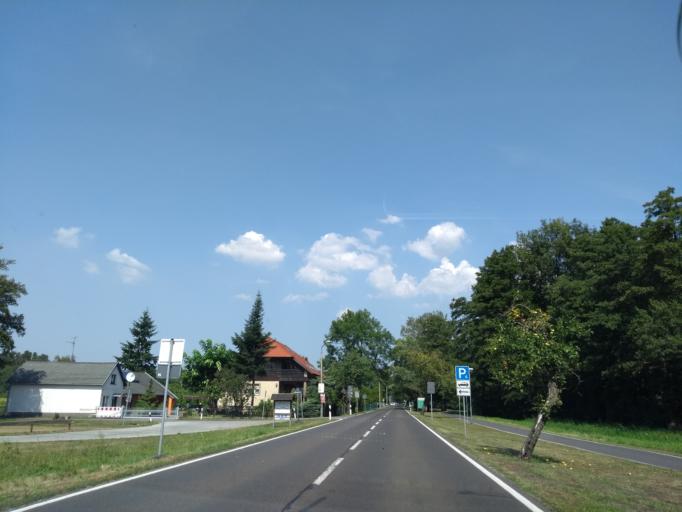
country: DE
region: Brandenburg
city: Burg
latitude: 51.8389
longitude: 14.1497
